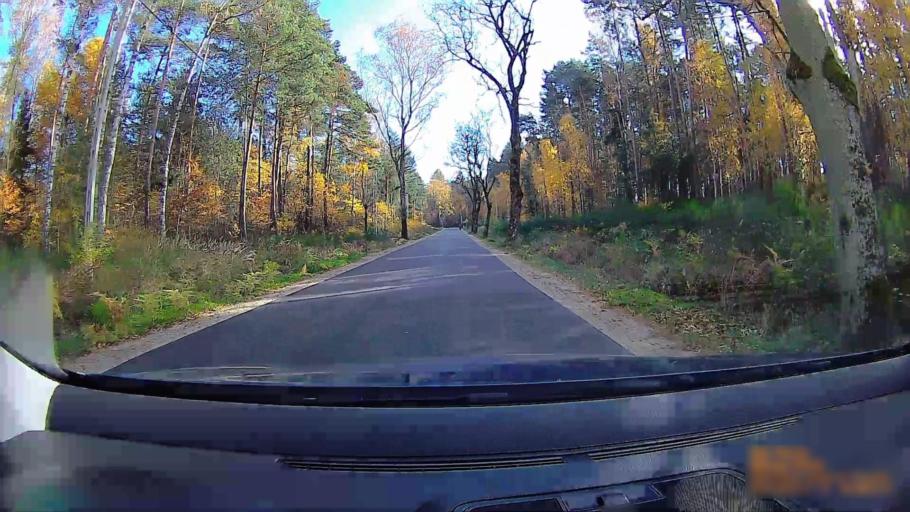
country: PL
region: Greater Poland Voivodeship
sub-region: Powiat ostrzeszowski
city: Ostrzeszow
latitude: 51.4075
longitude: 18.0013
